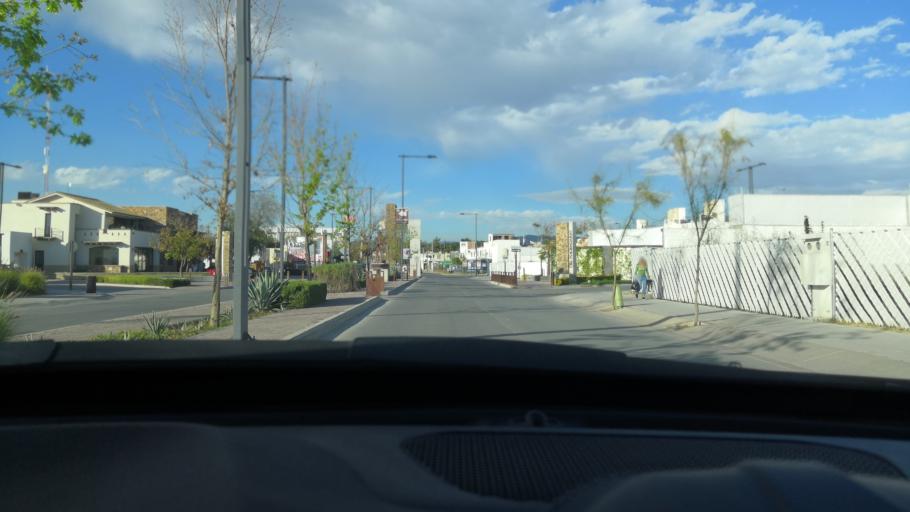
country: MX
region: Guanajuato
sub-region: Leon
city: San Jose de Duran (Los Troncoso)
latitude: 21.0871
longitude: -101.6528
